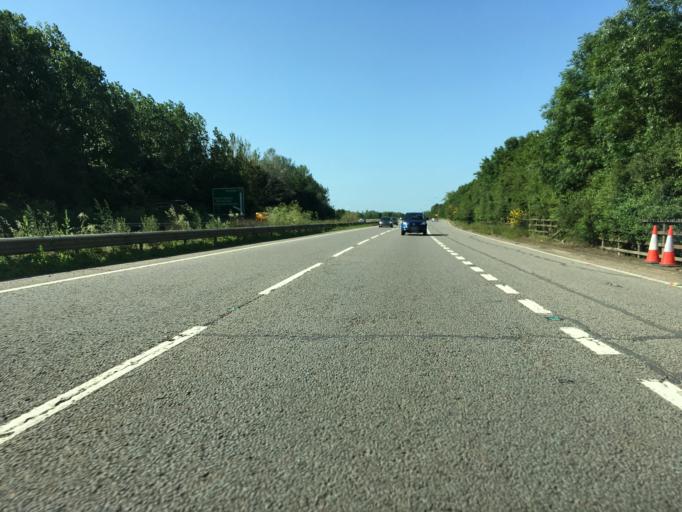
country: GB
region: England
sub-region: Milton Keynes
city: Simpson
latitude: 52.0031
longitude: -0.7096
